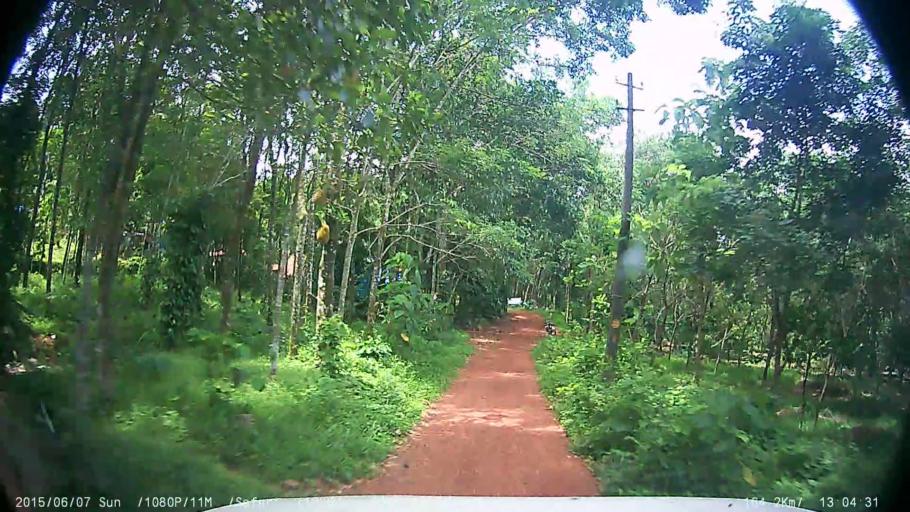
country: IN
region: Kerala
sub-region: Ernakulam
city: Muvattupuzha
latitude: 9.9288
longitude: 76.5672
